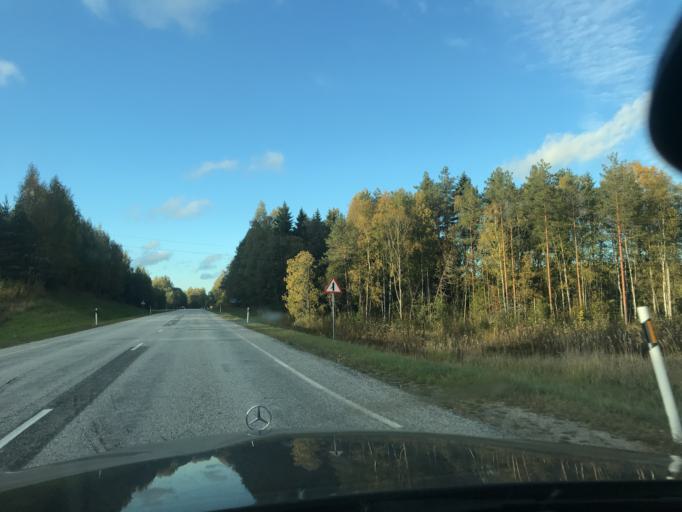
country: RU
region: Pskov
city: Pechory
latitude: 57.6744
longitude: 27.3275
